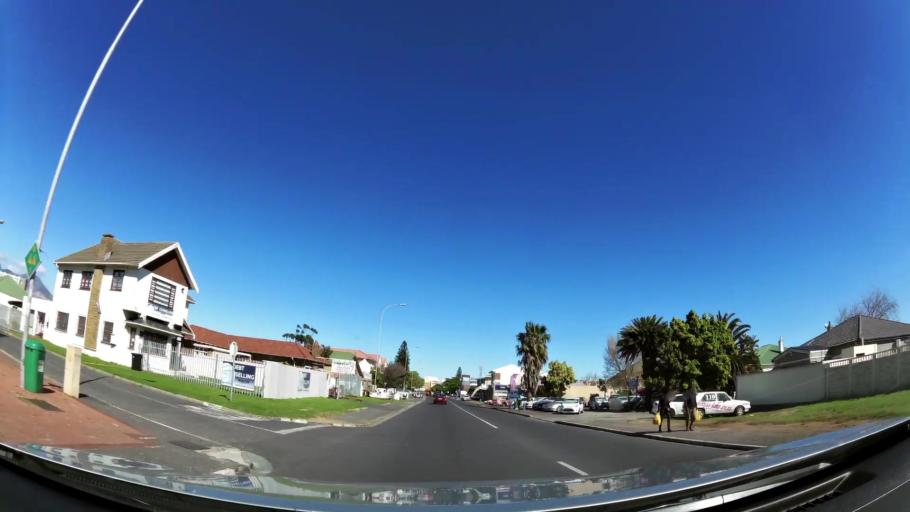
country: ZA
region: Western Cape
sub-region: Cape Winelands District Municipality
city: Stellenbosch
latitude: -34.1128
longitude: 18.8334
